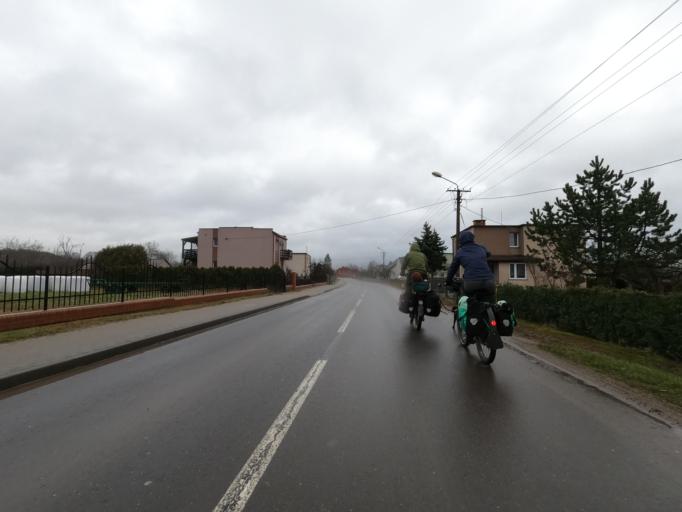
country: PL
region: Greater Poland Voivodeship
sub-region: Powiat pilski
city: Osiek nad Notecia
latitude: 53.1182
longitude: 17.2792
